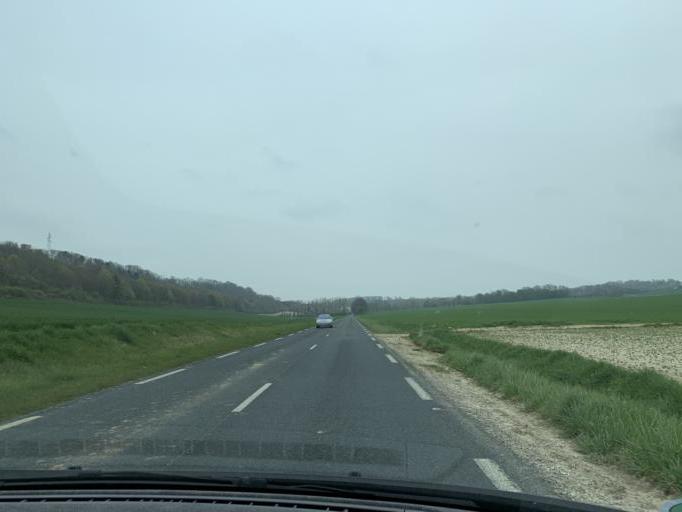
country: FR
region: Haute-Normandie
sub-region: Departement de la Seine-Maritime
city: Londinieres
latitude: 49.8417
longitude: 1.4303
